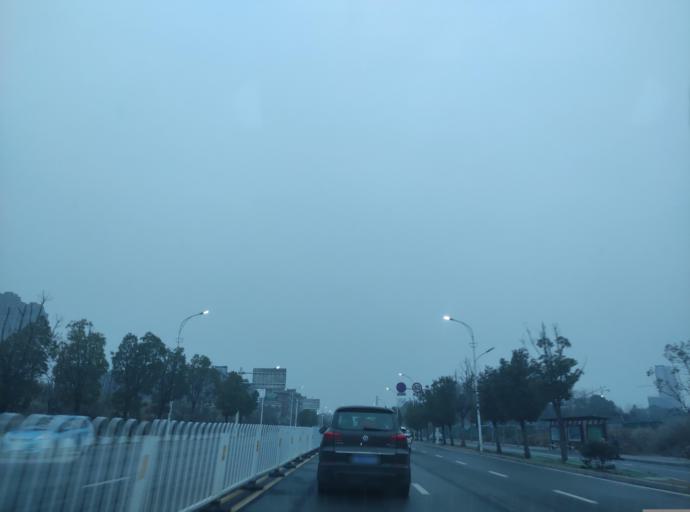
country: CN
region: Jiangxi Sheng
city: Pingxiang
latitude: 27.6686
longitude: 113.8630
